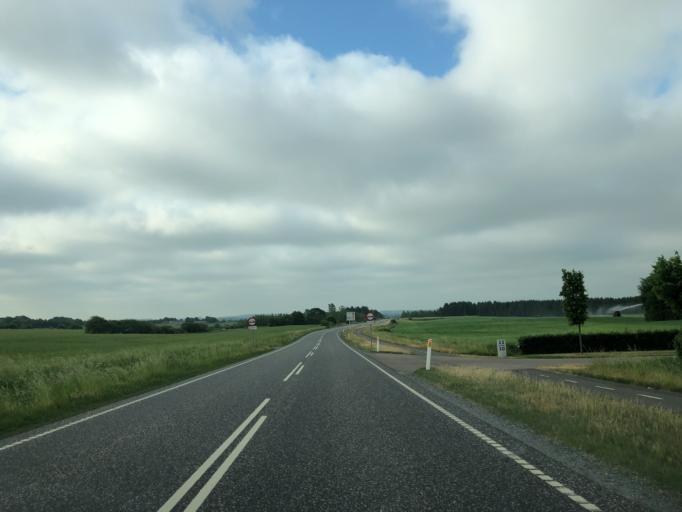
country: DK
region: South Denmark
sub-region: Vejle Kommune
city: Give
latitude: 55.8325
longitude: 9.2528
